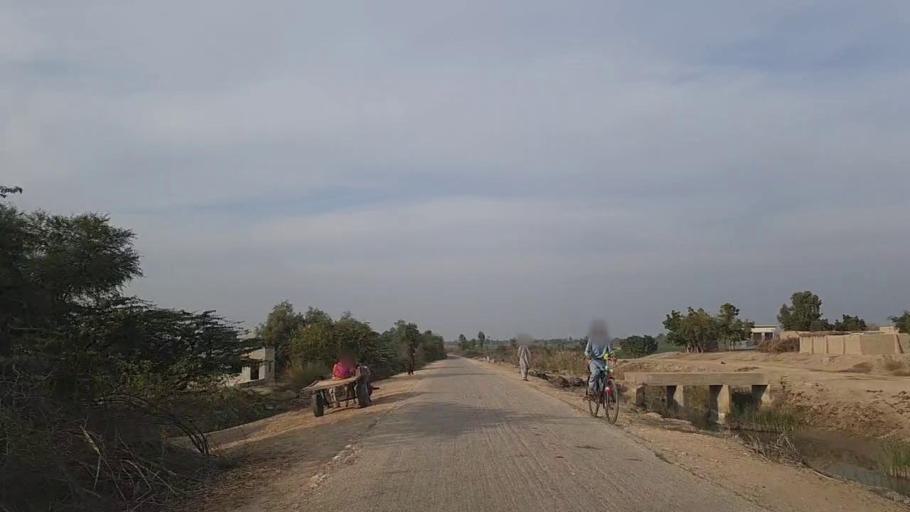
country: PK
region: Sindh
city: Daur
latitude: 26.4831
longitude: 68.4641
